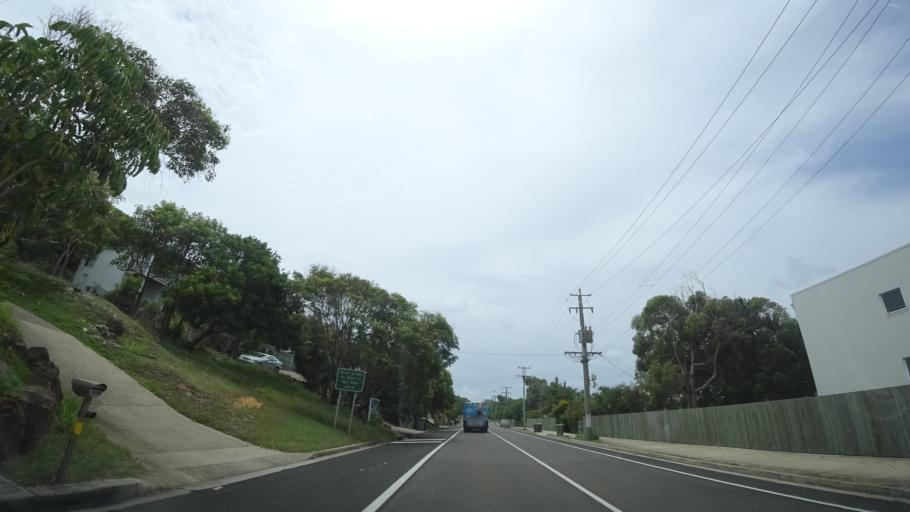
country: AU
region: Queensland
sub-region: Sunshine Coast
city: Coolum Beach
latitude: -26.5476
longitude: 153.1001
